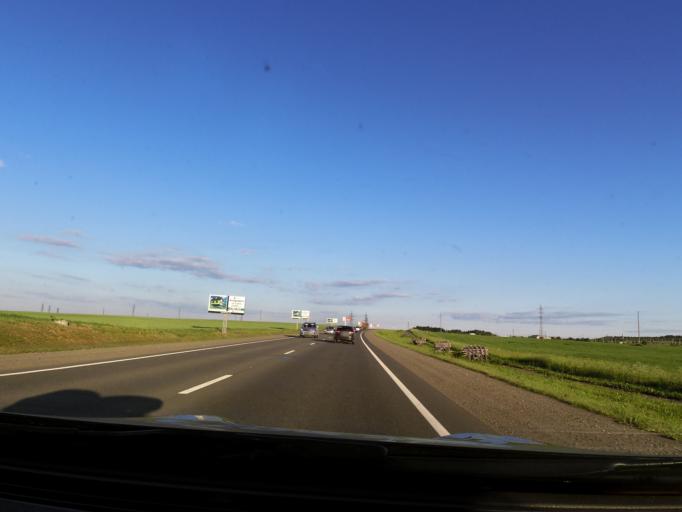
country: RU
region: Vologda
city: Vologda
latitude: 59.1637
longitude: 39.9219
